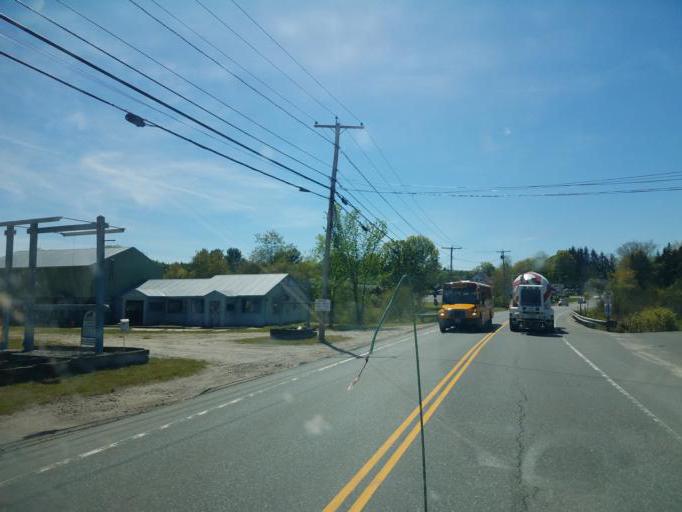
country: US
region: New Hampshire
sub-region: Grafton County
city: Enfield
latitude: 43.6427
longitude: -72.1255
